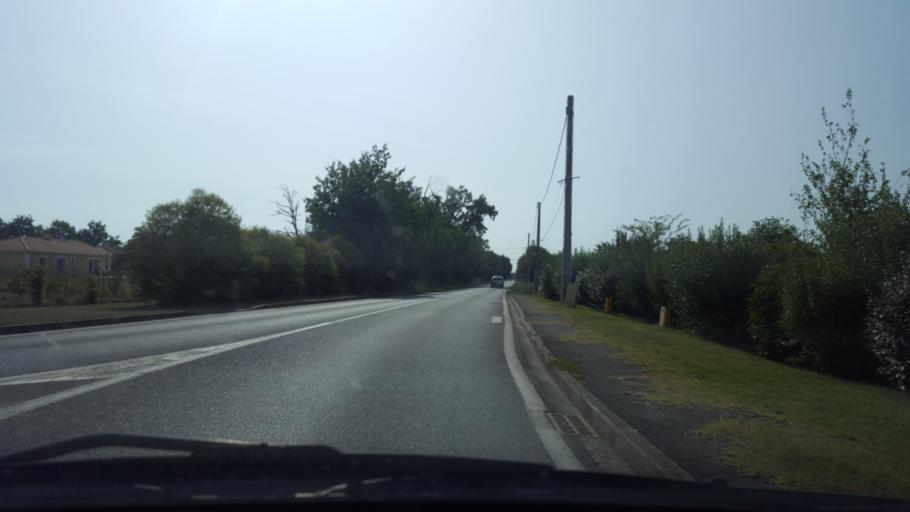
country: FR
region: Pays de la Loire
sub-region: Departement de la Loire-Atlantique
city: Montbert
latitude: 47.0578
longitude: -1.4972
